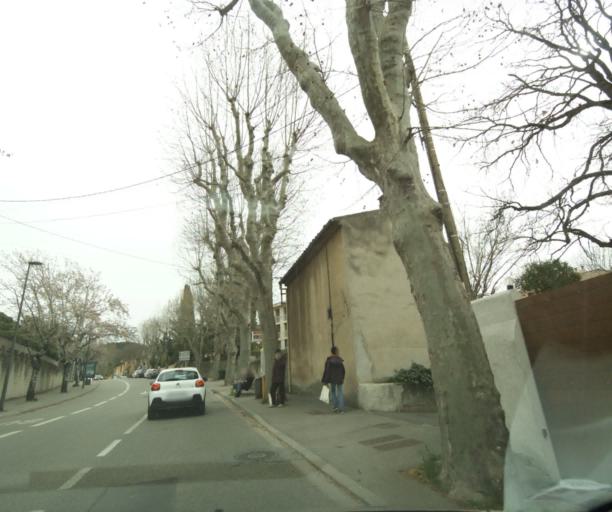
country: FR
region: Provence-Alpes-Cote d'Azur
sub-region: Departement des Bouches-du-Rhone
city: Aix-en-Provence
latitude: 43.5339
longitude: 5.4611
